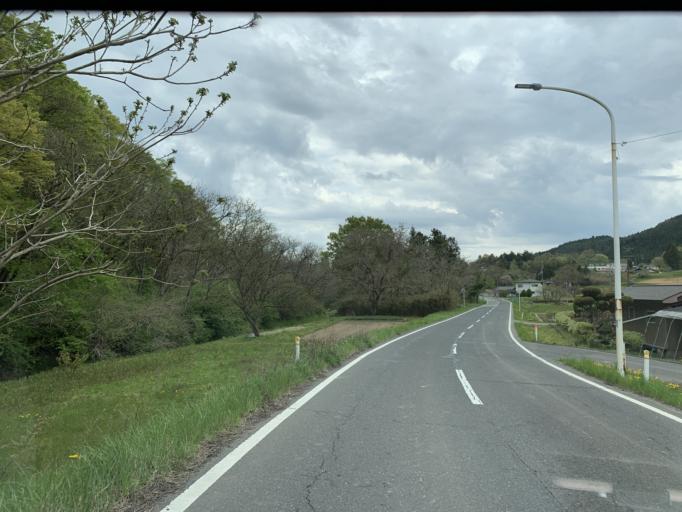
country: JP
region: Iwate
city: Ichinoseki
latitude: 38.7784
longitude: 141.3299
